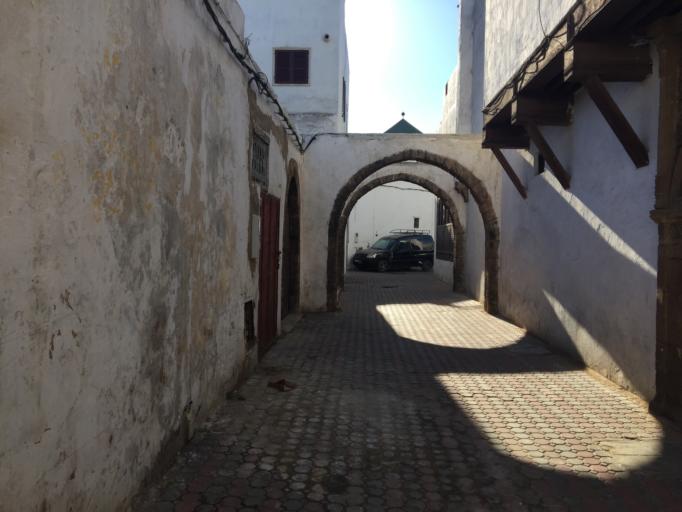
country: MA
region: Grand Casablanca
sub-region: Casablanca
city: Casablanca
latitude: 33.5767
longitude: -7.6052
